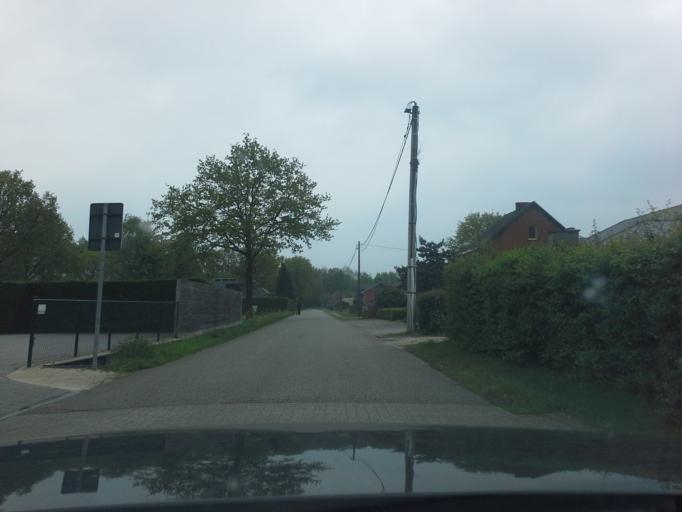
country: BE
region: Flanders
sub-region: Provincie Antwerpen
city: Geel
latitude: 51.1797
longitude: 4.9984
